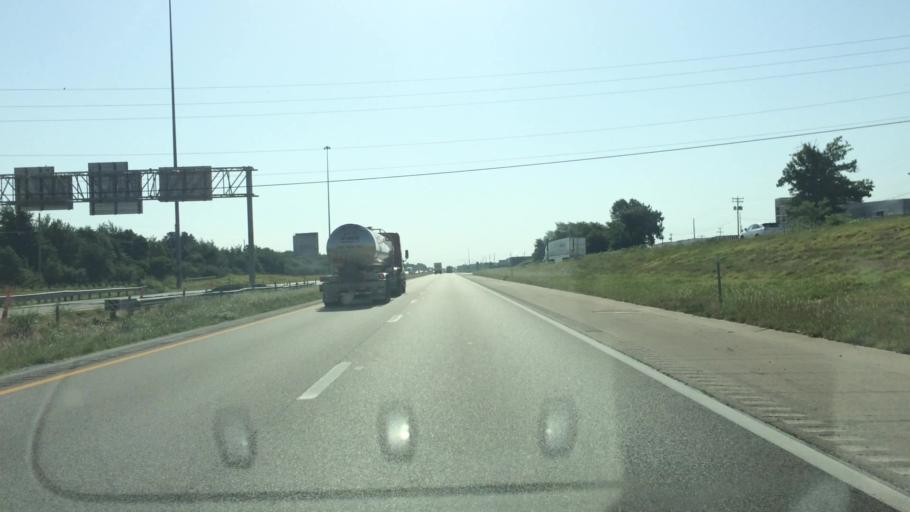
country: US
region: Missouri
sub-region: Greene County
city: Springfield
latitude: 37.2501
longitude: -93.2211
